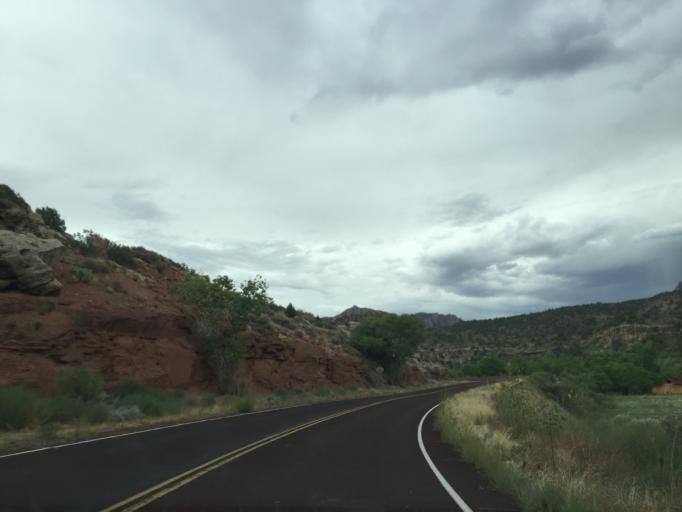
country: US
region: Utah
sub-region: Washington County
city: Hildale
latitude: 37.1626
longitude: -113.0229
